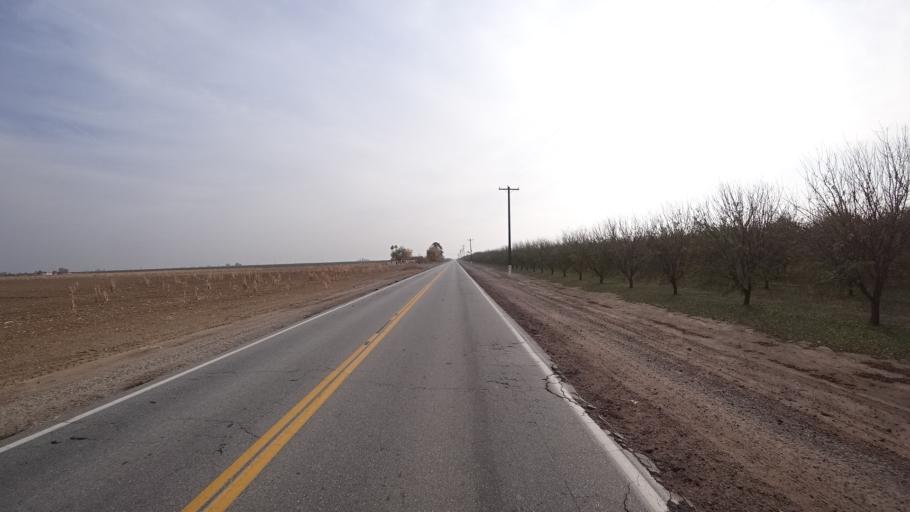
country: US
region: California
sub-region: Kern County
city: Greenacres
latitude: 35.2876
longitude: -119.1283
